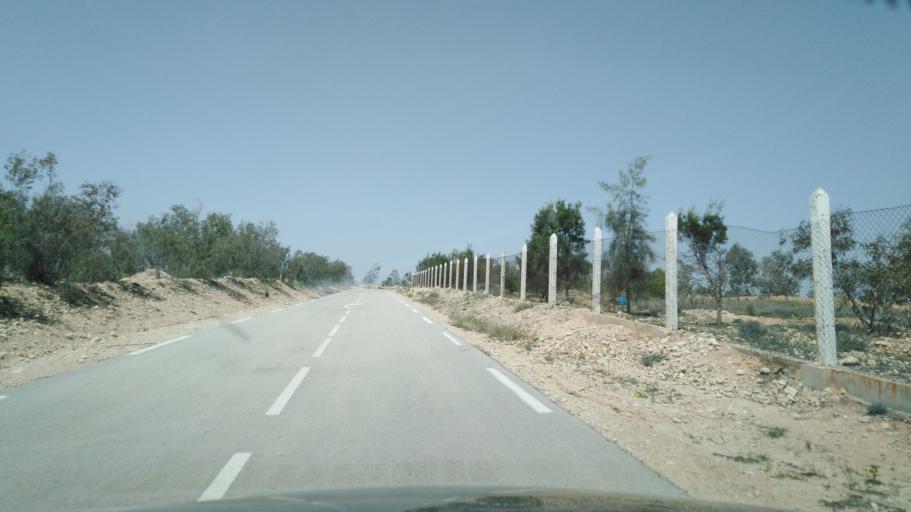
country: TN
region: Safaqis
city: Sfax
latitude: 34.7073
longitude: 10.5236
